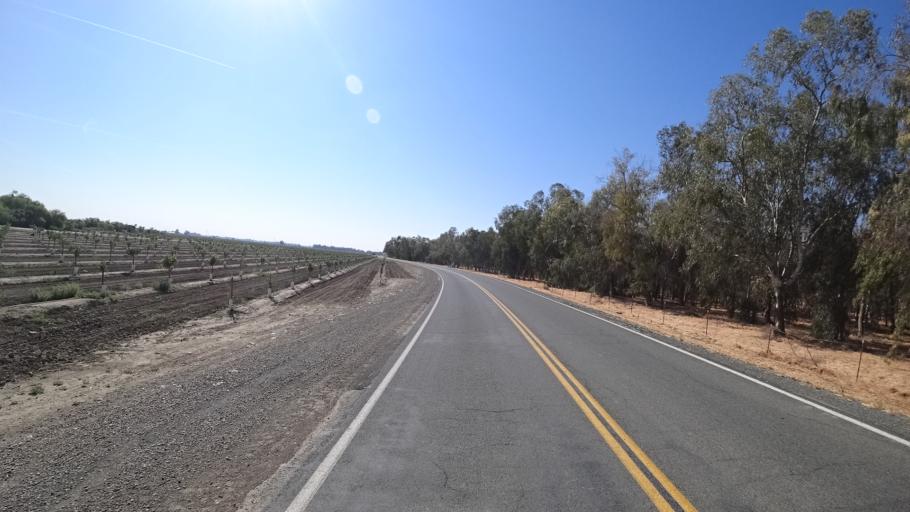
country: US
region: California
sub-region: Fresno County
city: Riverdale
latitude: 36.3629
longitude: -119.9156
